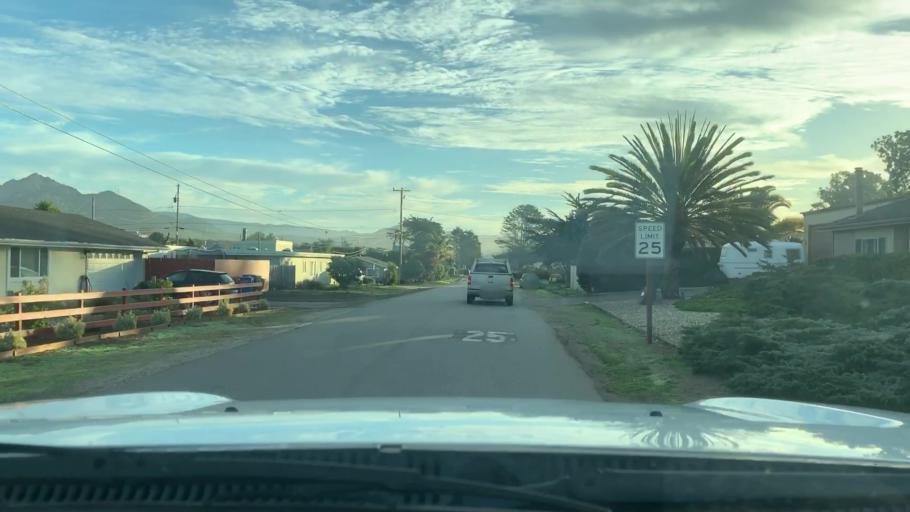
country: US
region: California
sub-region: San Luis Obispo County
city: Los Osos
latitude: 35.3243
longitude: -120.8277
